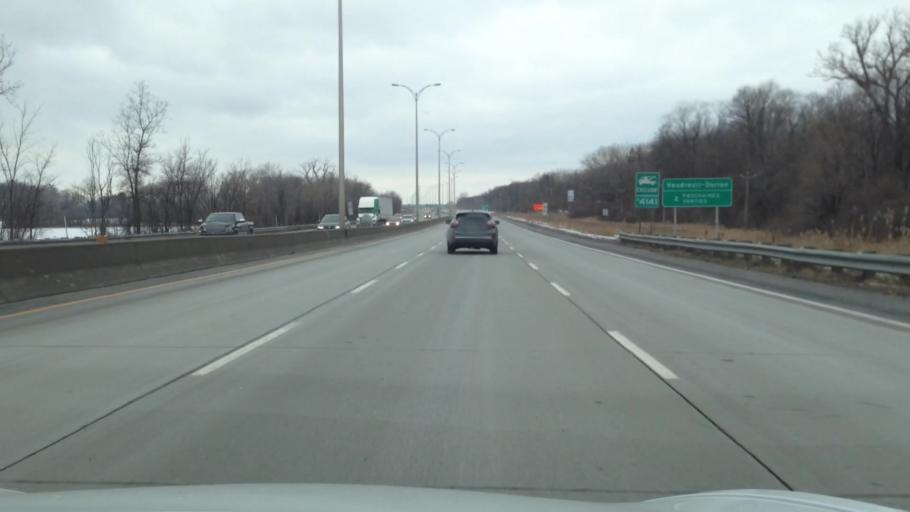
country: CA
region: Quebec
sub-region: Monteregie
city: Pincourt
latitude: 45.4195
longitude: -73.9947
